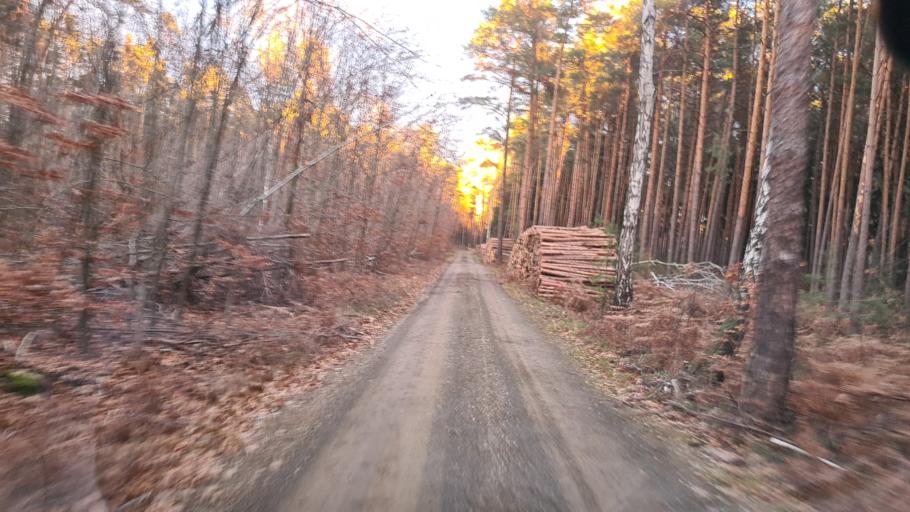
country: DE
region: Brandenburg
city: Schonborn
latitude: 51.5798
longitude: 13.4780
